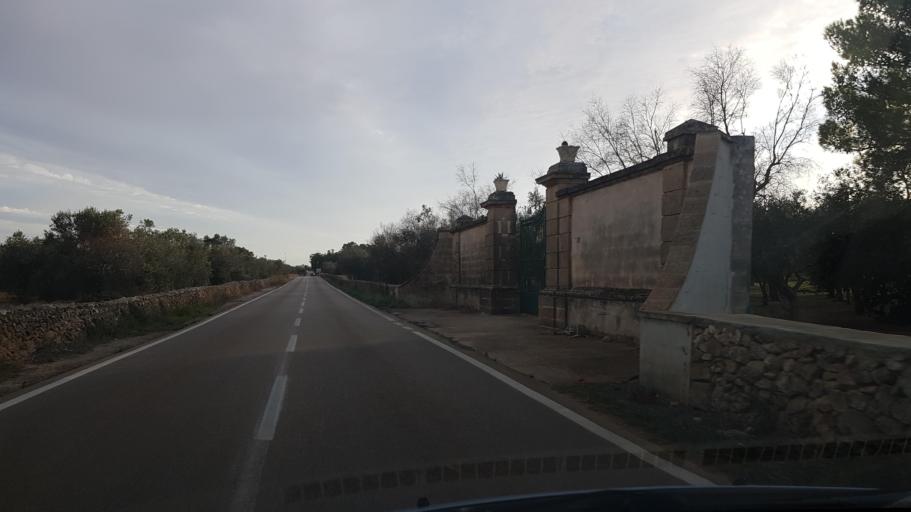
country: IT
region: Apulia
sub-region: Provincia di Brindisi
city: Torchiarolo
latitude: 40.4631
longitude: 18.1169
